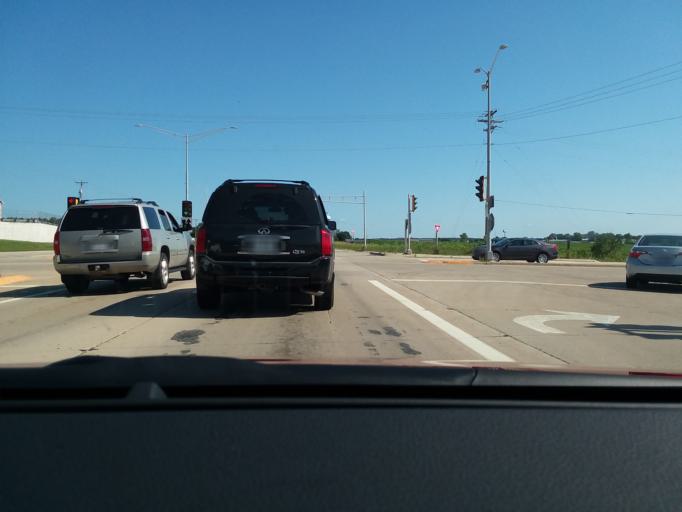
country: US
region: Wisconsin
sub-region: Dane County
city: Windsor
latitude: 43.1641
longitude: -89.3242
